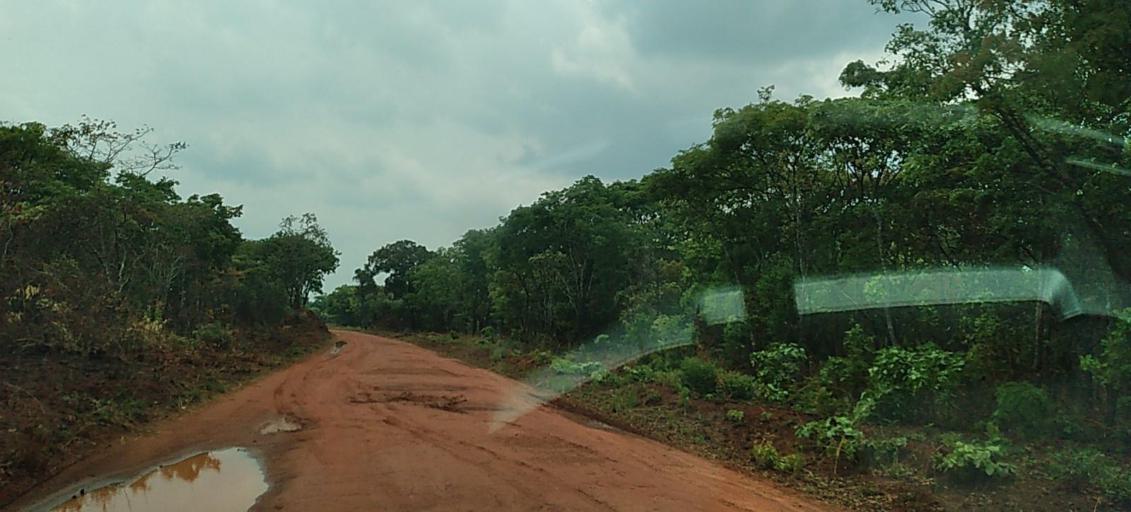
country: ZM
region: North-Western
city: Mwinilunga
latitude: -11.5559
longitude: 24.7731
